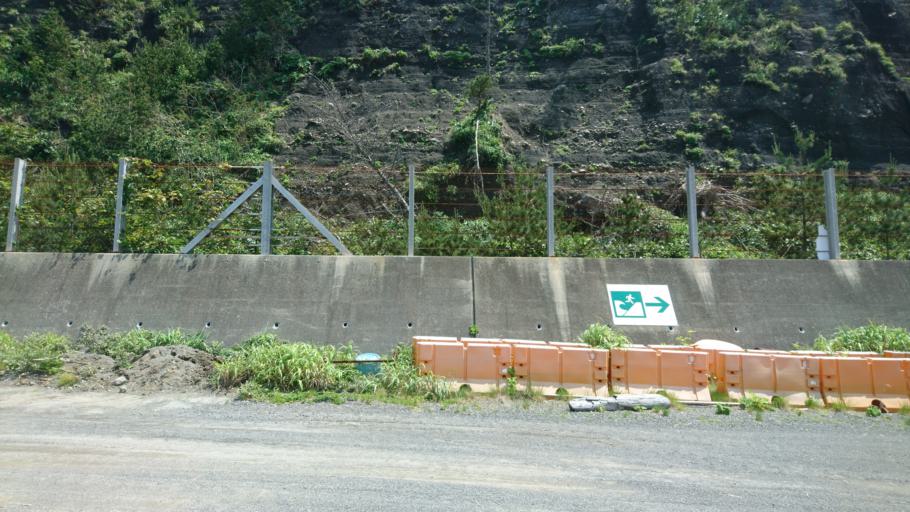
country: JP
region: Shizuoka
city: Shimoda
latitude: 34.4156
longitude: 139.2767
